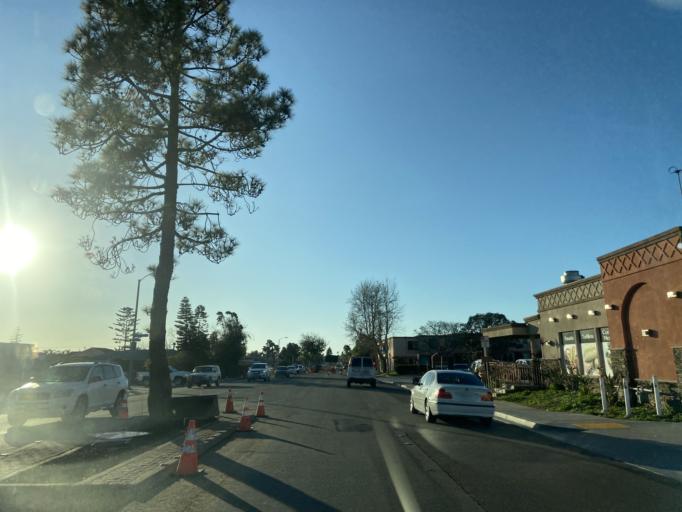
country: US
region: California
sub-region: San Diego County
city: Imperial Beach
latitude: 32.5766
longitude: -117.1062
